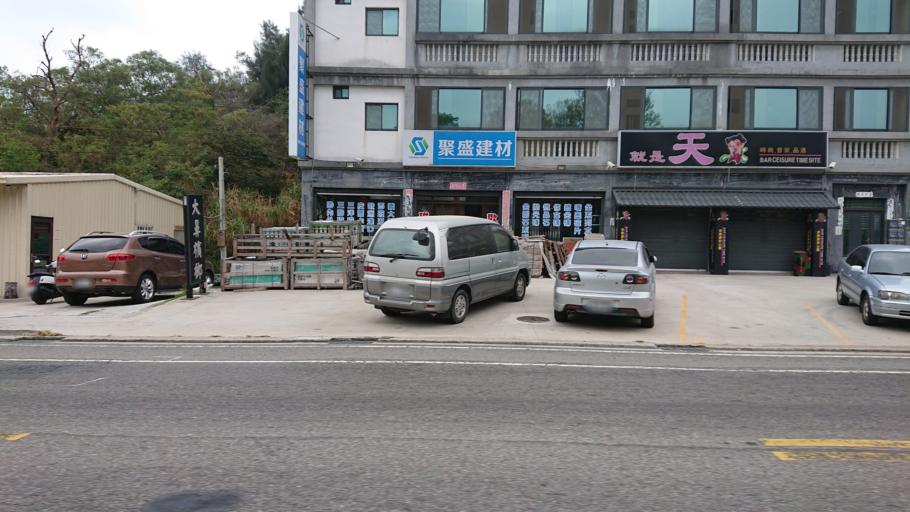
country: TW
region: Fukien
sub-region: Kinmen
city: Jincheng
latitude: 24.4419
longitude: 118.3903
